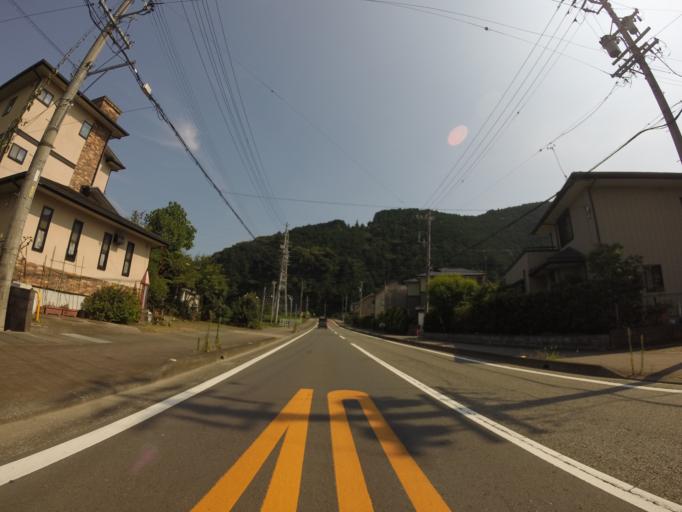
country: JP
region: Shizuoka
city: Shizuoka-shi
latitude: 35.0426
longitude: 138.3660
